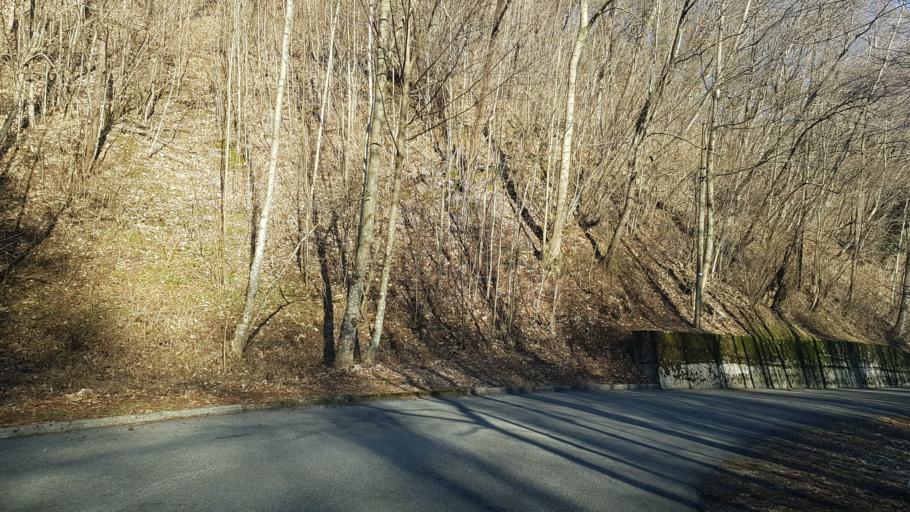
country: IT
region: Friuli Venezia Giulia
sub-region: Provincia di Udine
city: Isola
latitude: 46.2656
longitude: 13.1998
